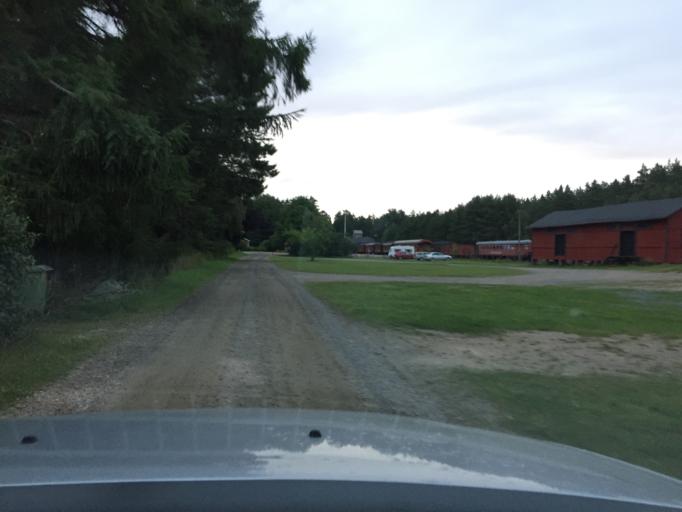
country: SE
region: Skane
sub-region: Kristianstads Kommun
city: Degeberga
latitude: 55.7336
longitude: 14.1247
